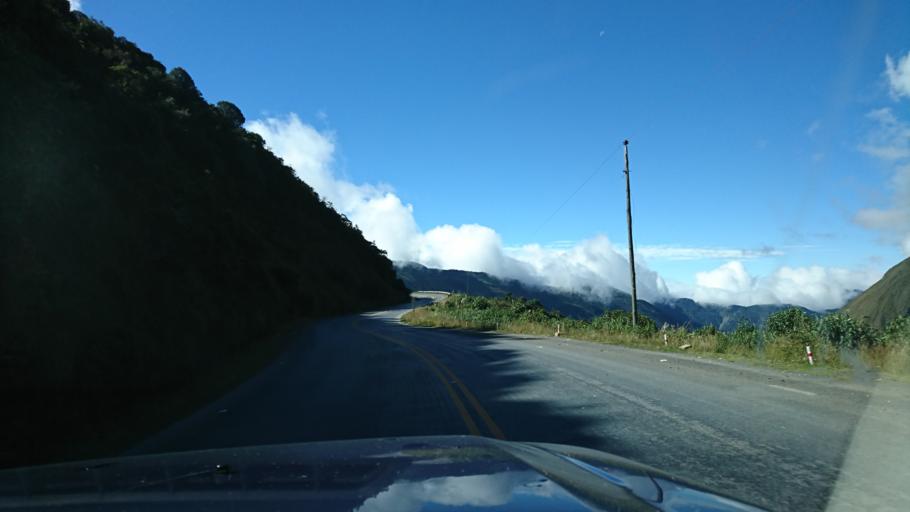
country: BO
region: La Paz
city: Coroico
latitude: -16.3071
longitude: -67.8986
